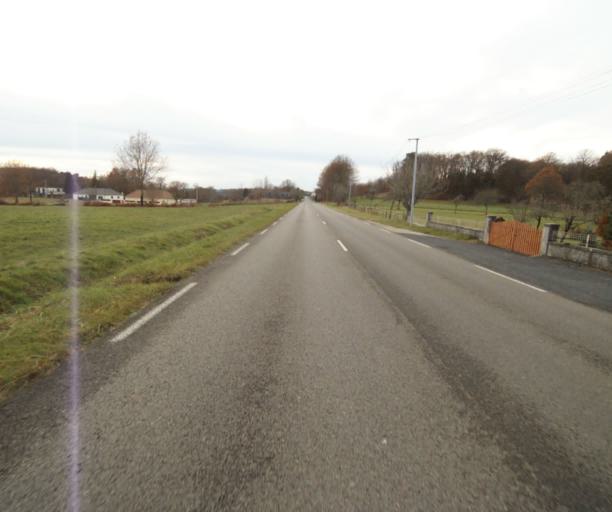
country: FR
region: Limousin
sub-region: Departement de la Correze
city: Saint-Mexant
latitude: 45.2680
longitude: 1.6582
